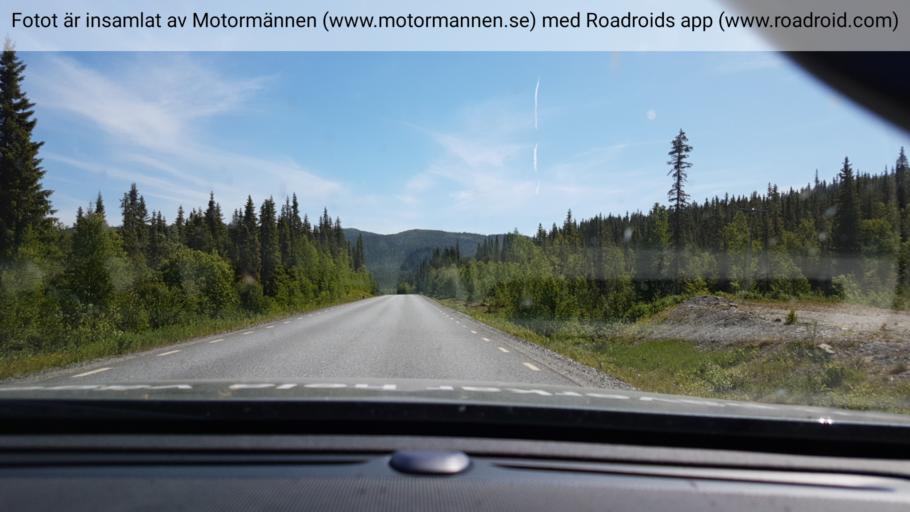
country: SE
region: Vaesterbotten
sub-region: Vilhelmina Kommun
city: Sjoberg
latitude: 64.7317
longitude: 15.3626
